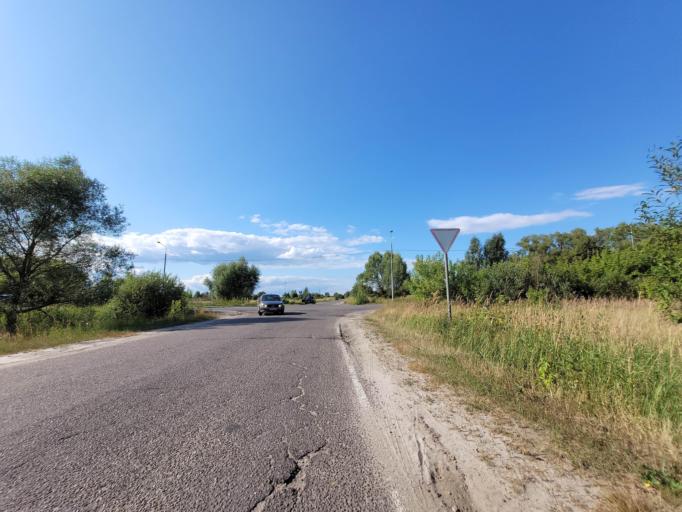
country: RU
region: Moskovskaya
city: Konobeyevo
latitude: 55.4041
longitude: 38.7078
